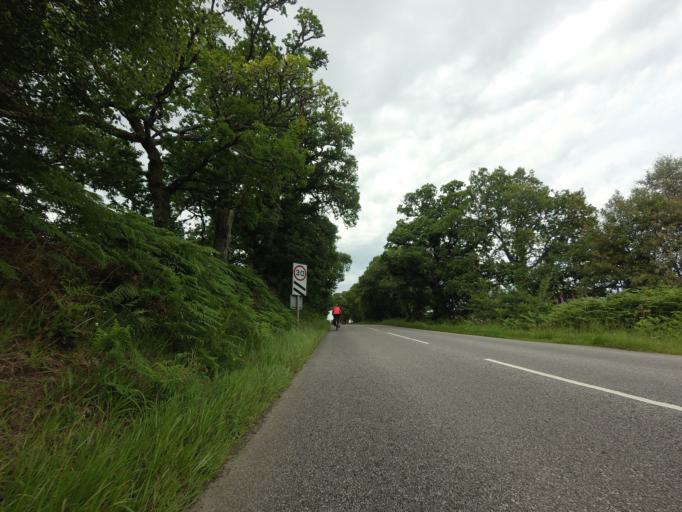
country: GB
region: Scotland
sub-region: Highland
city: Alness
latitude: 57.8770
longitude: -4.3584
